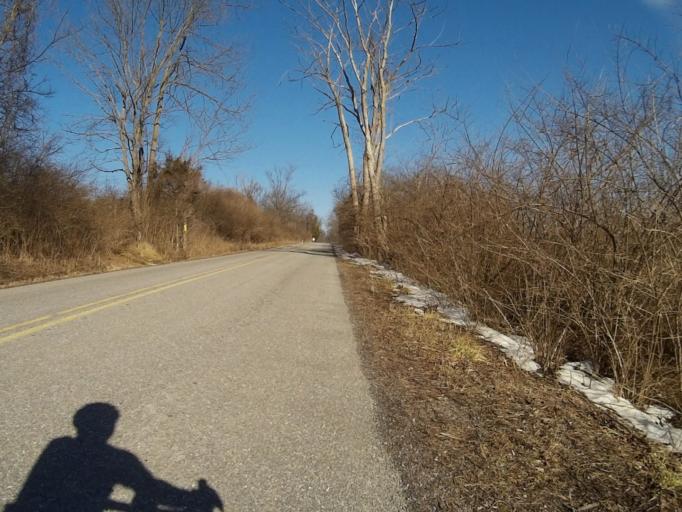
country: US
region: Pennsylvania
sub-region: Centre County
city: Park Forest Village
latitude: 40.8684
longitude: -77.8848
